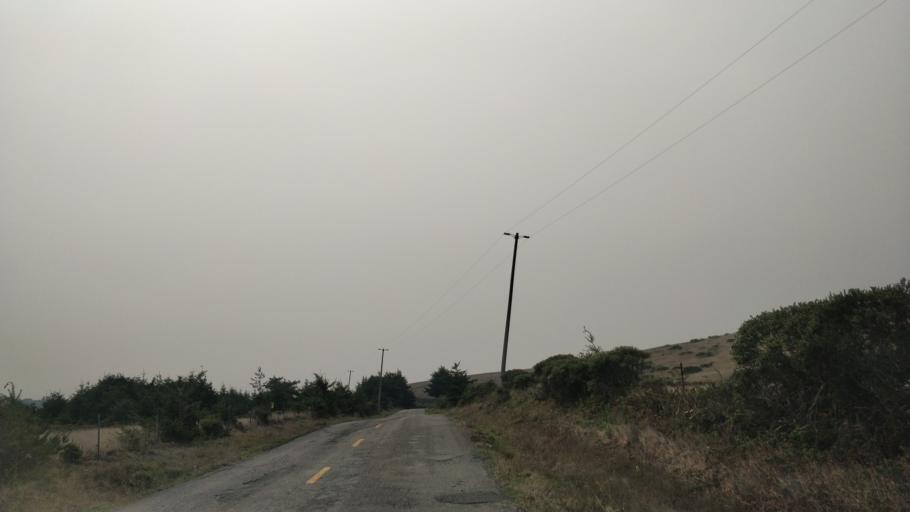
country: US
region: California
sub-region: Humboldt County
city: Ferndale
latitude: 40.4427
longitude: -124.3816
